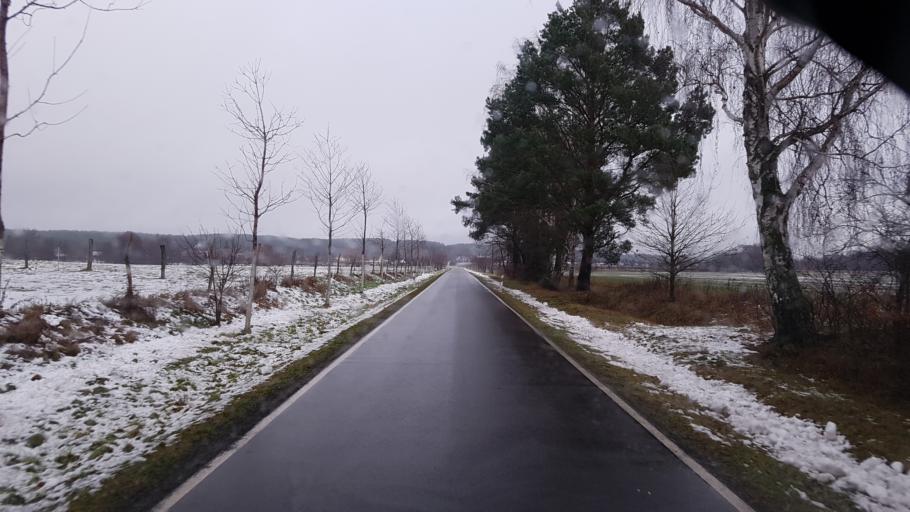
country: DE
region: Brandenburg
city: Neu Zauche
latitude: 51.9423
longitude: 14.1098
